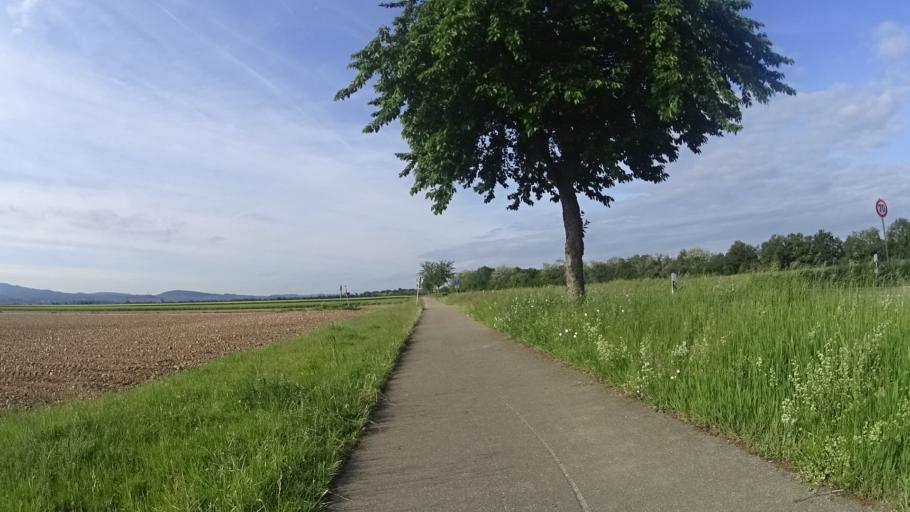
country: FR
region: Alsace
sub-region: Departement du Haut-Rhin
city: Blodelsheim
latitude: 47.8642
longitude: 7.5867
